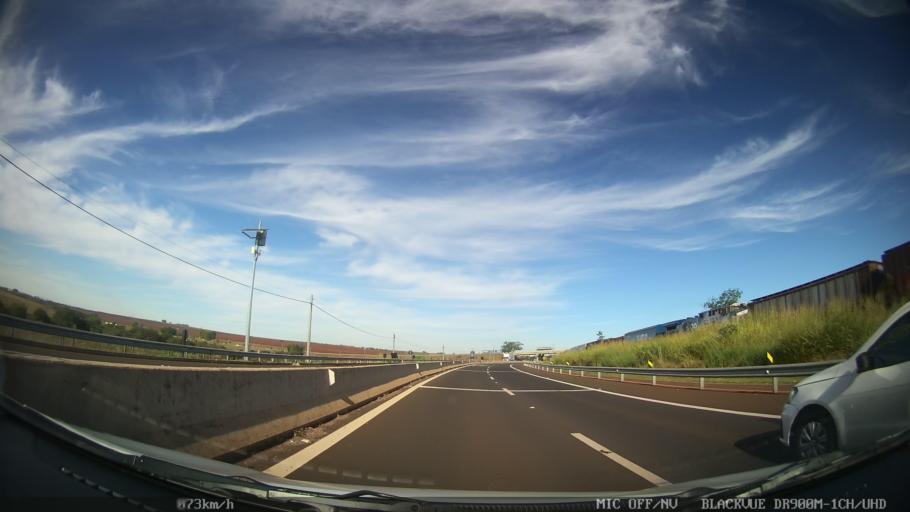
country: BR
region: Sao Paulo
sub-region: Araraquara
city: Araraquara
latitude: -21.7918
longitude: -48.1348
